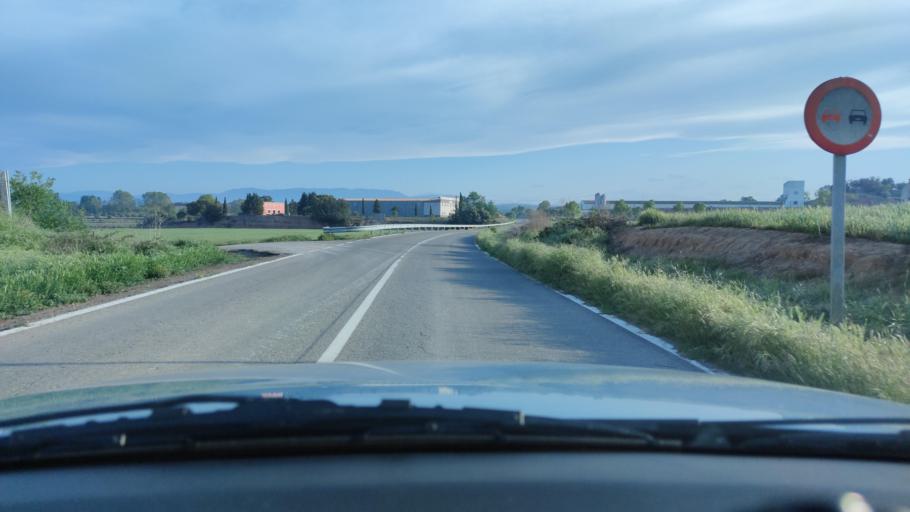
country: ES
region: Catalonia
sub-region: Provincia de Lleida
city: Agramunt
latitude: 41.7992
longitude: 1.0534
